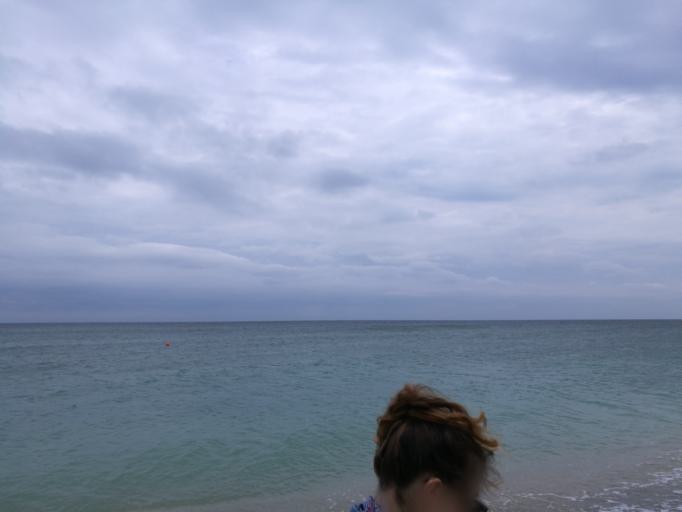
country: RO
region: Constanta
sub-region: Municipiul Mangalia
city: Mangalia
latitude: 43.7528
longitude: 28.5757
